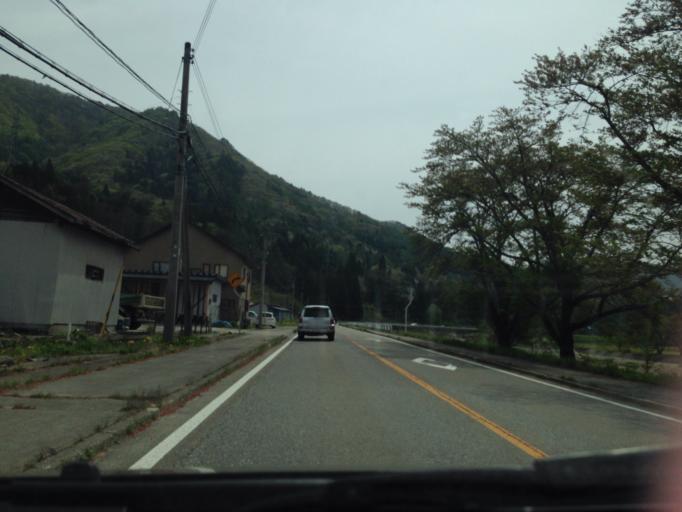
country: JP
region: Tochigi
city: Kuroiso
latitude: 37.1426
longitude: 139.7303
